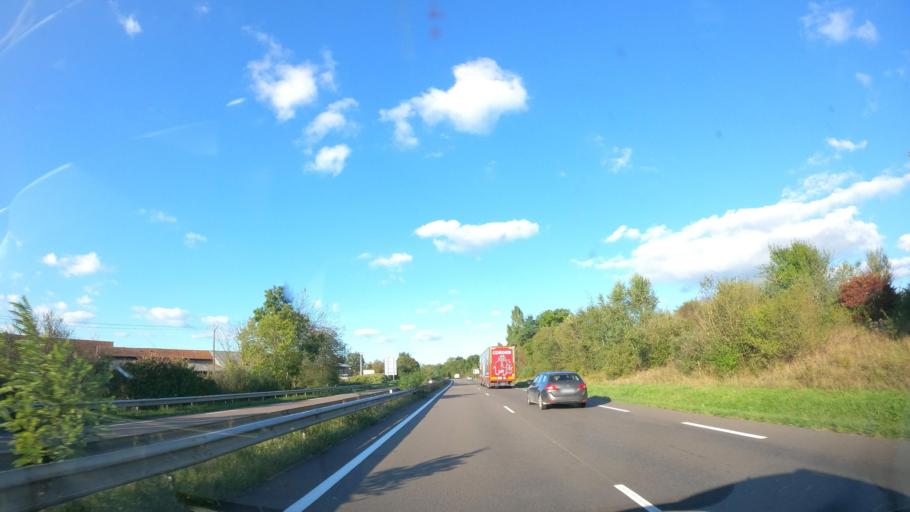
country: FR
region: Bourgogne
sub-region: Departement de Saone-et-Loire
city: Montceau-les-Mines
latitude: 46.6710
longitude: 4.3439
